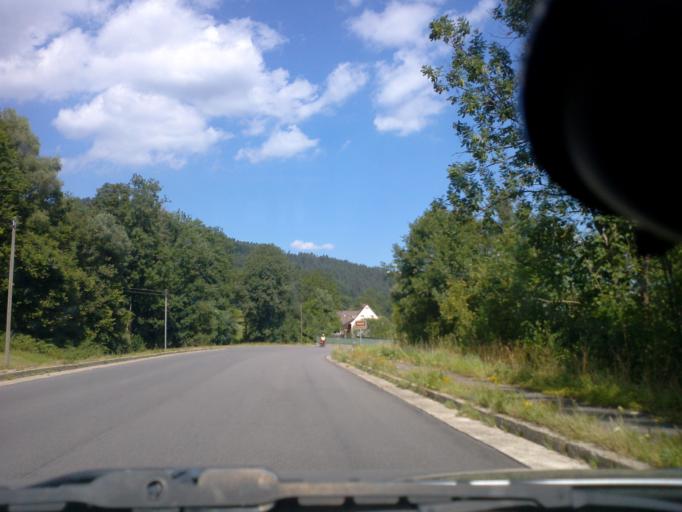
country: DE
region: Baden-Wuerttemberg
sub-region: Freiburg Region
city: Gutach (Schwarzwaldbahn)
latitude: 48.2302
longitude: 8.2178
